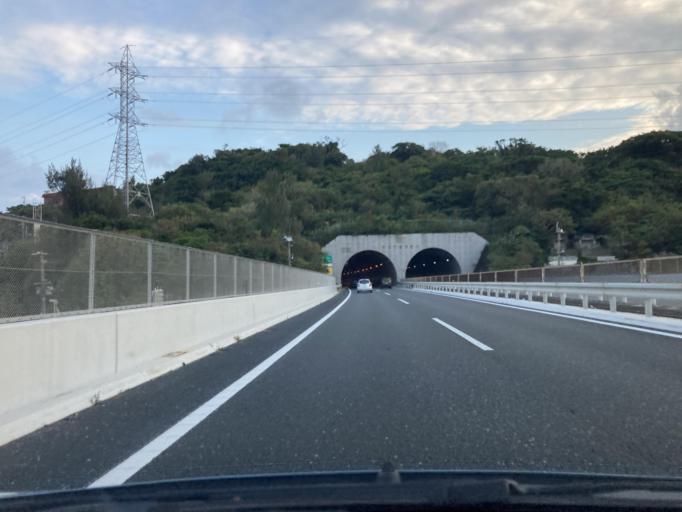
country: JP
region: Okinawa
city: Chatan
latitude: 26.3096
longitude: 127.7881
